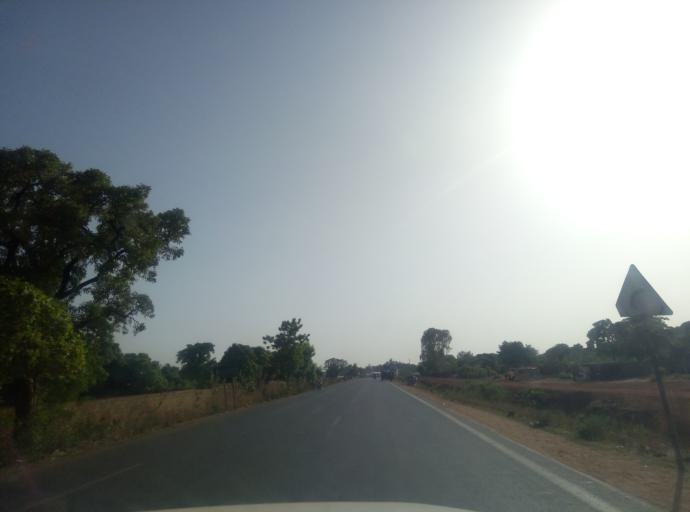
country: ML
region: Bamako
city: Bamako
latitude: 12.5809
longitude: -7.7771
